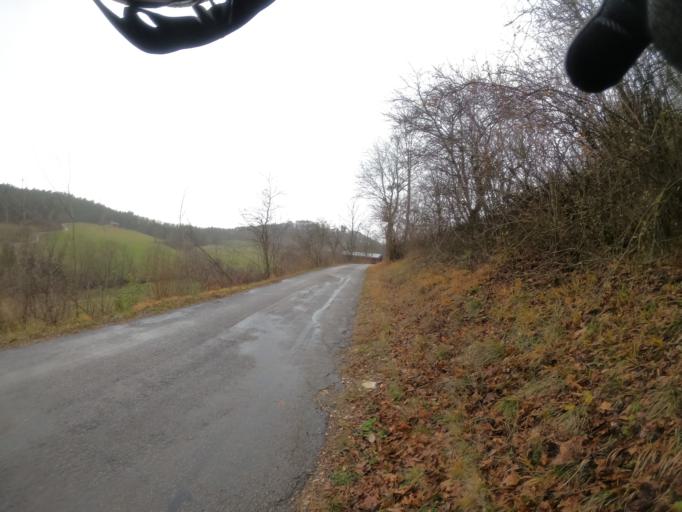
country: DE
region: Baden-Wuerttemberg
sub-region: Regierungsbezirk Stuttgart
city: Waldstetten
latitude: 48.7262
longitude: 9.8421
